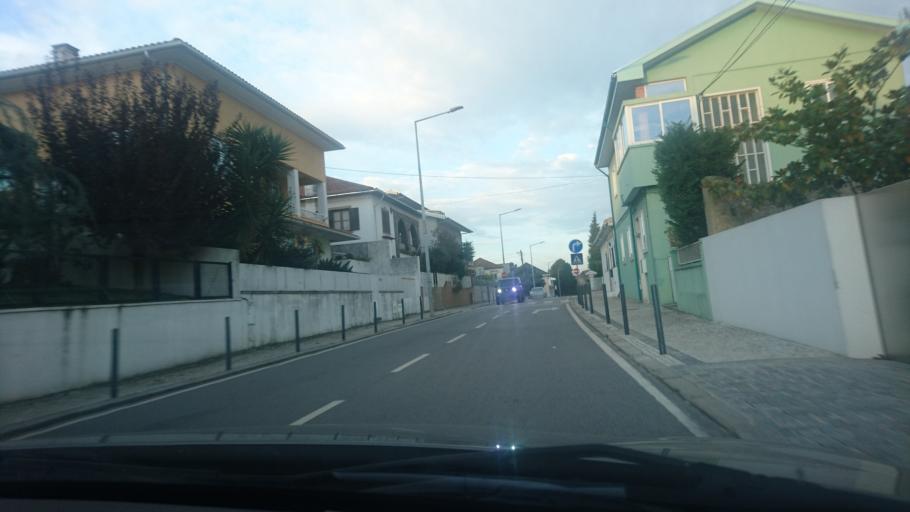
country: PT
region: Aveiro
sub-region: Sao Joao da Madeira
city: Sao Joao da Madeira
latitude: 40.8932
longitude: -8.4905
